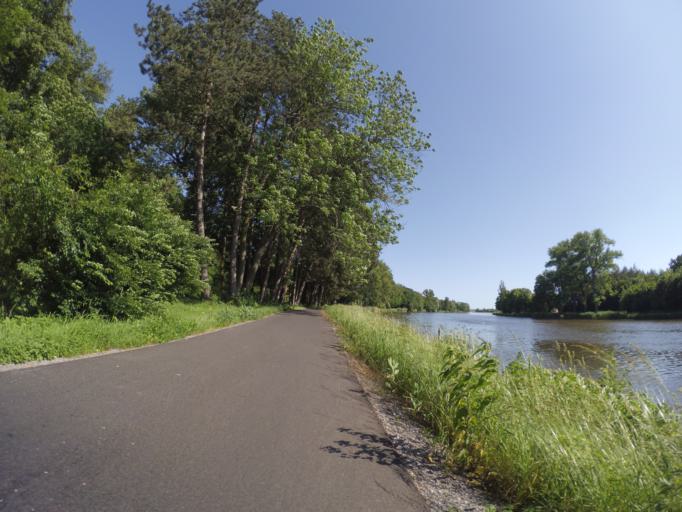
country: CZ
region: Central Bohemia
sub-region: Okres Nymburk
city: Nymburk
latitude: 50.1782
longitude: 15.0740
